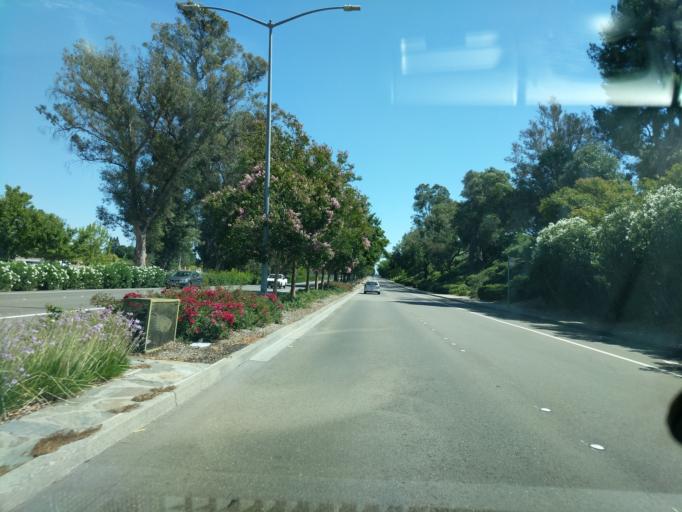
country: US
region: California
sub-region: Contra Costa County
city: San Ramon
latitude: 37.7549
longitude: -121.9627
